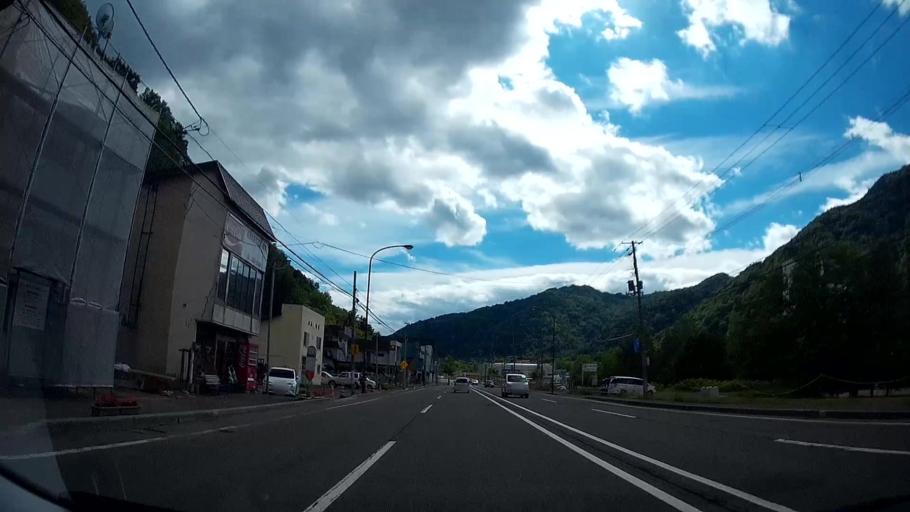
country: JP
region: Hokkaido
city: Sapporo
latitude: 42.9633
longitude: 141.1624
